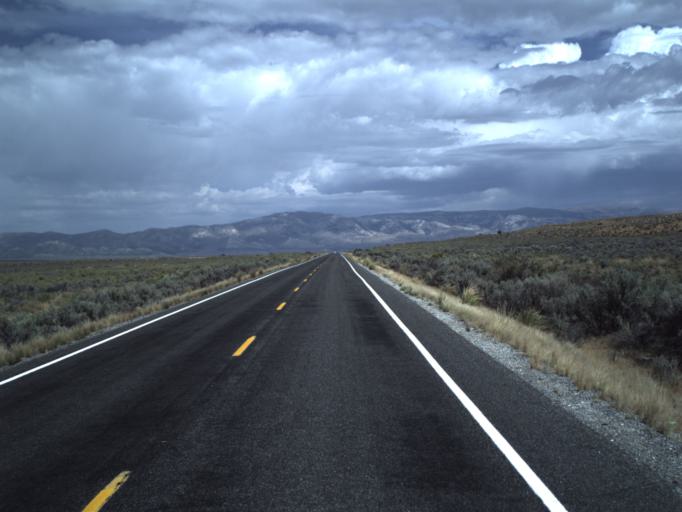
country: US
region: Idaho
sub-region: Cassia County
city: Burley
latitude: 41.6797
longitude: -113.5410
